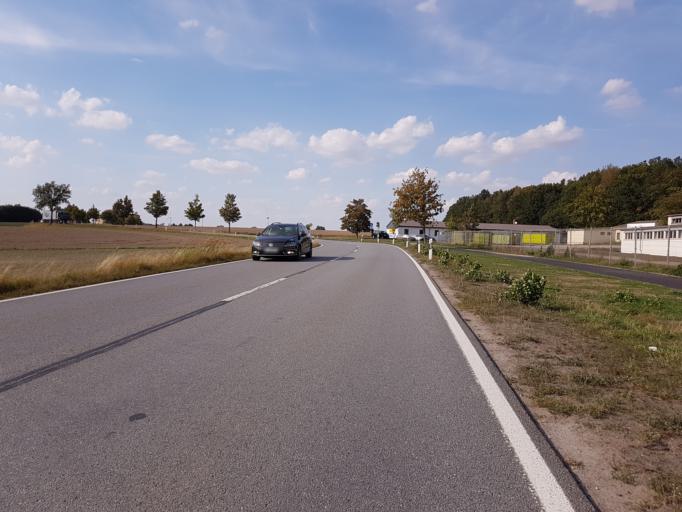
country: DE
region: Saxony
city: Claussnitz
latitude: 50.9449
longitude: 12.8717
